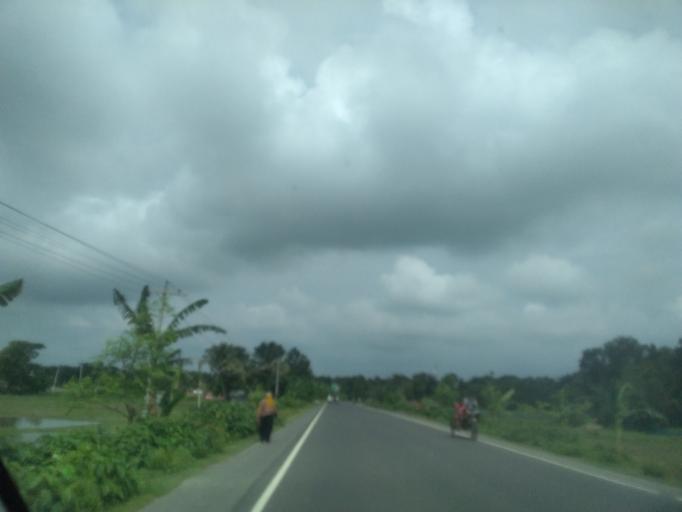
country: BD
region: Khulna
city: Kesabpur
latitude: 22.8371
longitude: 89.3042
